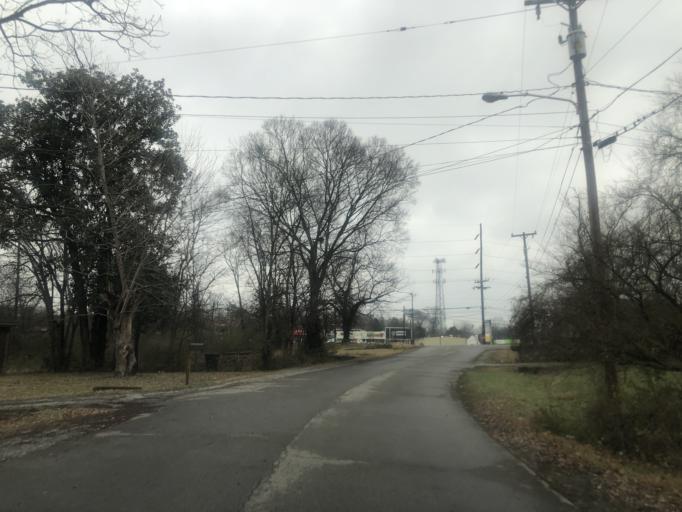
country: US
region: Tennessee
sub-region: Davidson County
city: Lakewood
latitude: 36.1519
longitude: -86.6679
